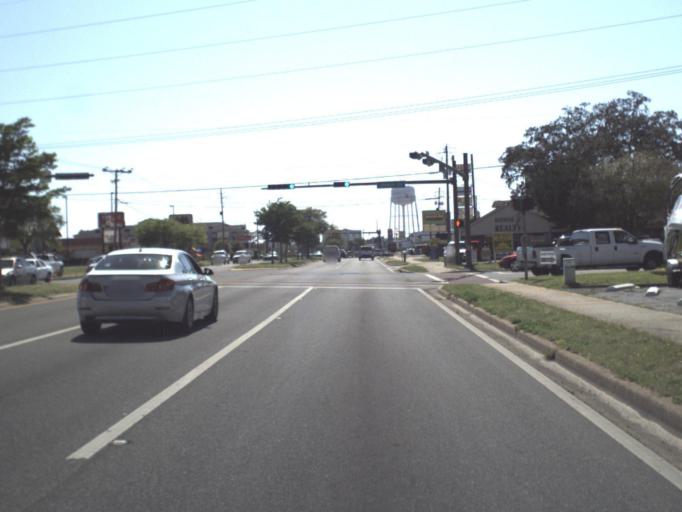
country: US
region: Florida
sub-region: Okaloosa County
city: Mary Esther
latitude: 30.4245
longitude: -86.6464
